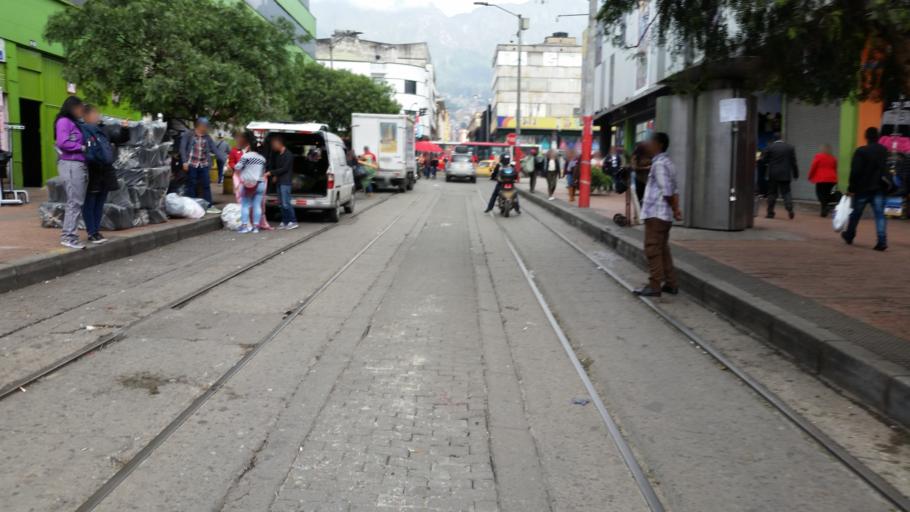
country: CO
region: Bogota D.C.
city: Bogota
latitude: 4.5995
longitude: -74.0792
